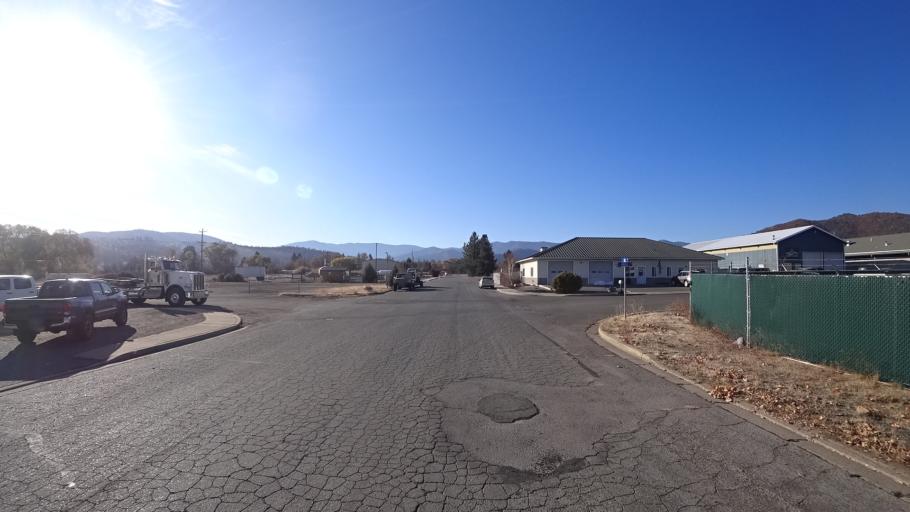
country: US
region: California
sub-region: Siskiyou County
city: Yreka
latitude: 41.7137
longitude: -122.6385
